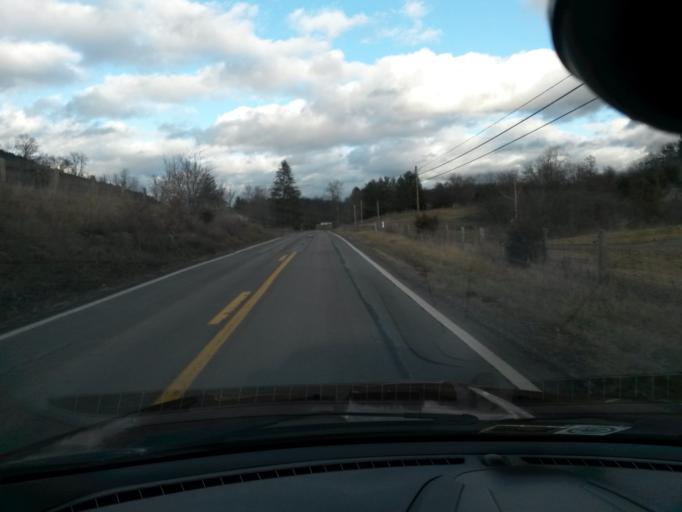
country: US
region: West Virginia
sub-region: Monroe County
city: Union
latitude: 37.5726
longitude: -80.5555
